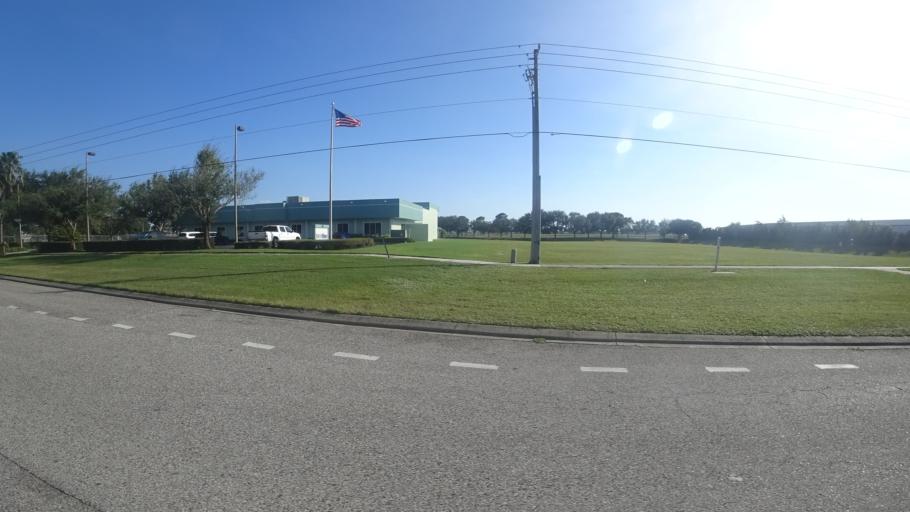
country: US
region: Florida
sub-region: Manatee County
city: Whitfield
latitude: 27.4076
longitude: -82.5603
